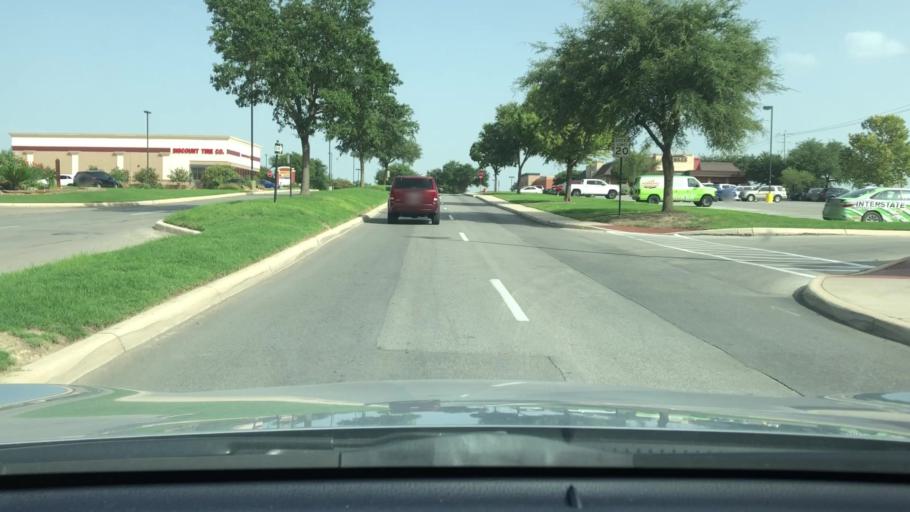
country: US
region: Texas
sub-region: Bexar County
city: Live Oak
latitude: 29.5634
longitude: -98.3325
